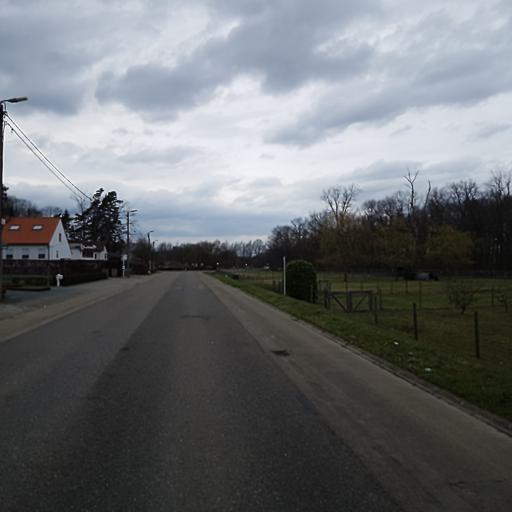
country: BE
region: Flanders
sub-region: Provincie Vlaams-Brabant
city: Begijnendijk
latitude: 50.9702
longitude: 4.7817
